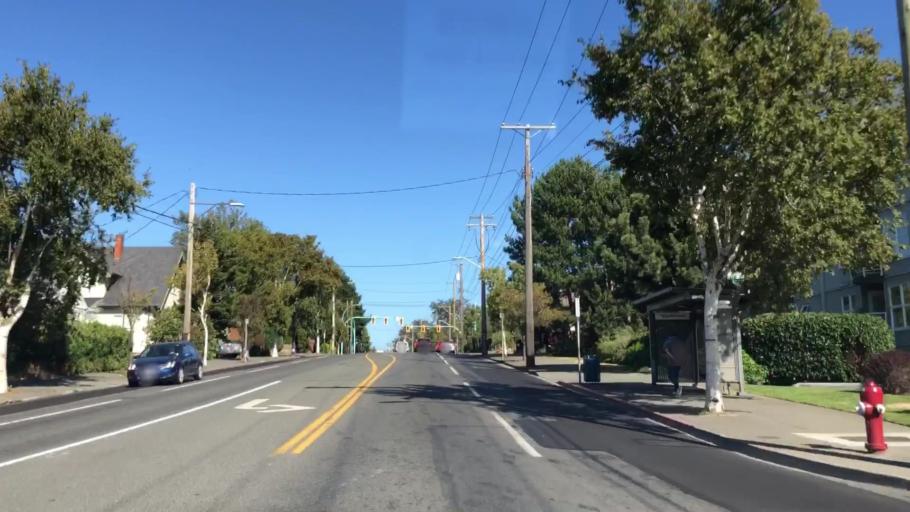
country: CA
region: British Columbia
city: Victoria
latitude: 48.4401
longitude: -123.3538
